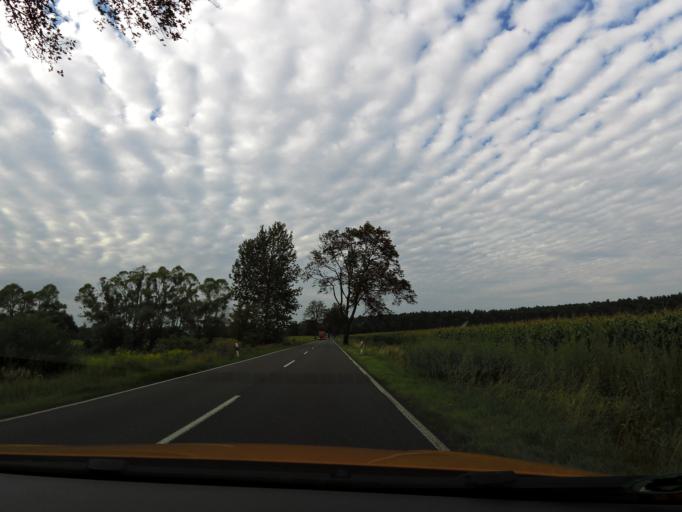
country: DE
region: Brandenburg
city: Brandenburg an der Havel
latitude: 52.3672
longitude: 12.5963
